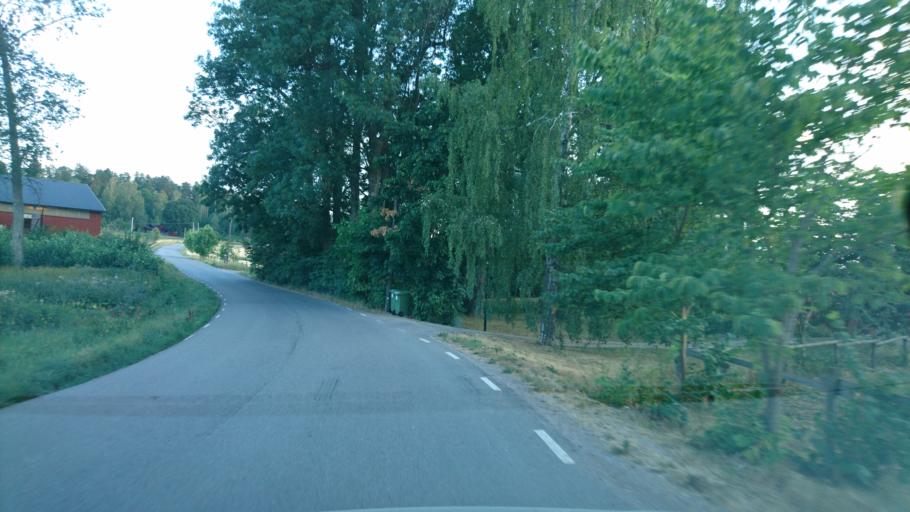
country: SE
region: Uppsala
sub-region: Uppsala Kommun
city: Saevja
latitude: 59.8131
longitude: 17.6804
